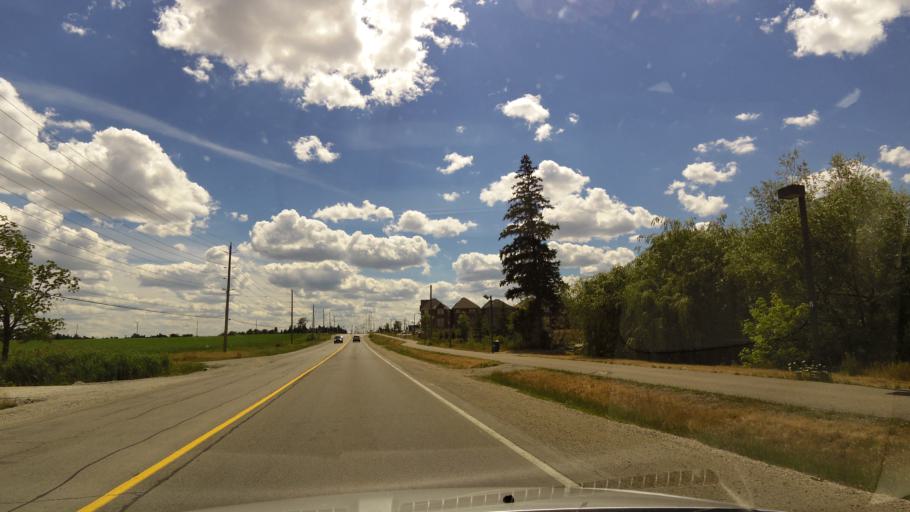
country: CA
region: Ontario
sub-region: Halton
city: Milton
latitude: 43.6209
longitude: -79.8808
